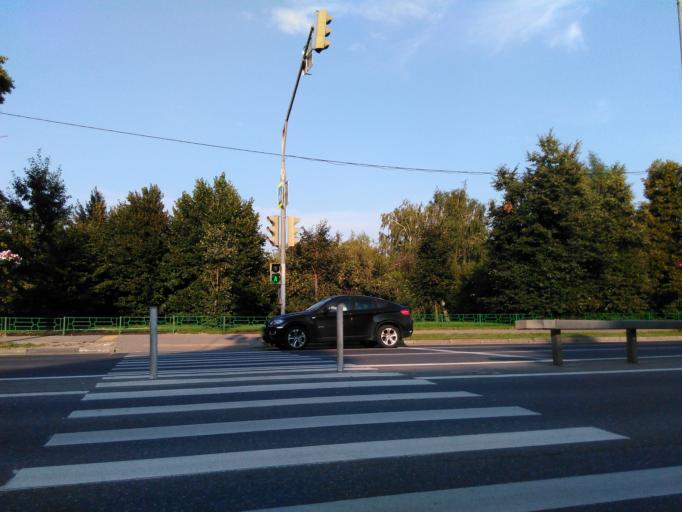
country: RU
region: Moskovskaya
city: Kastanayevo
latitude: 55.7199
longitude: 37.5008
